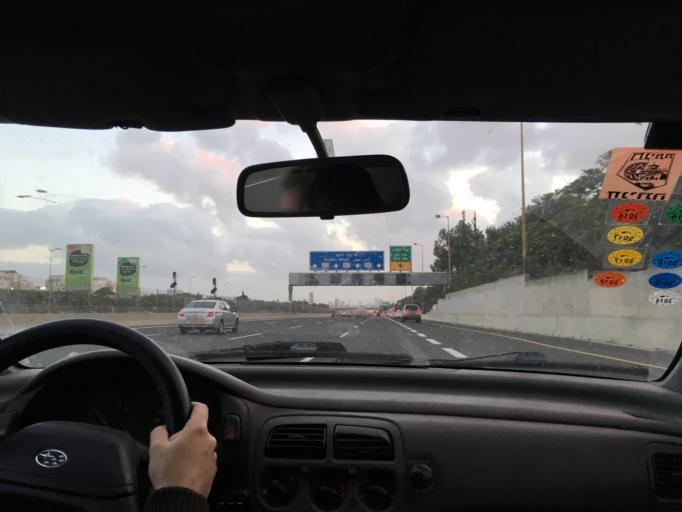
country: IL
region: Tel Aviv
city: Ramat HaSharon
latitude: 32.1272
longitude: 34.8099
